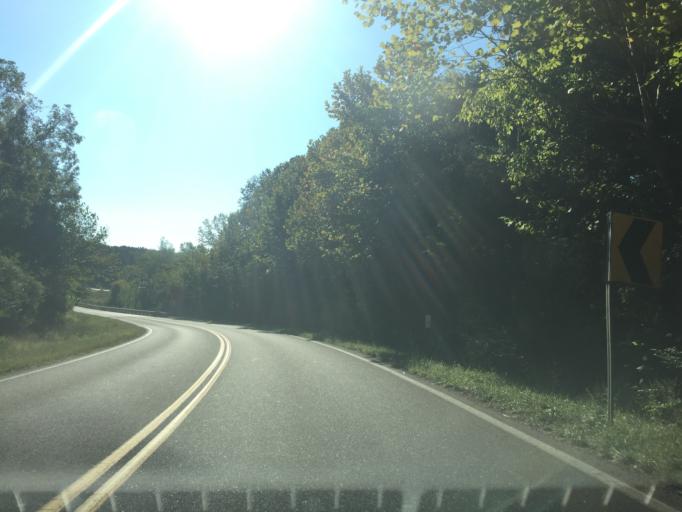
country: US
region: Tennessee
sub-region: Hamilton County
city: Harrison
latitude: 35.0841
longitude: -85.1603
